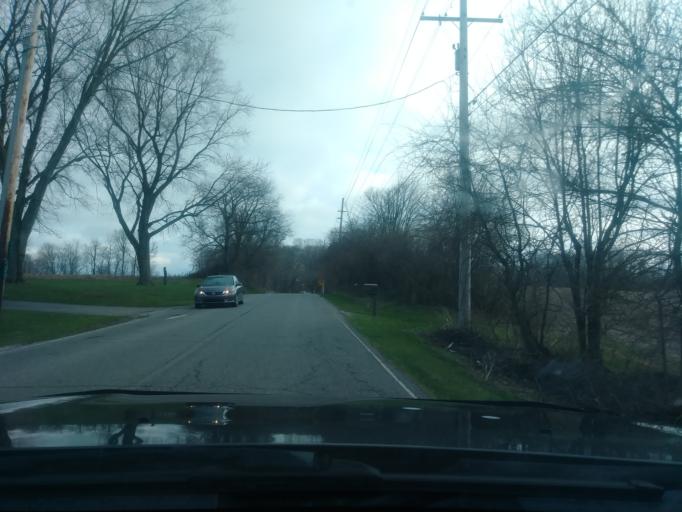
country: US
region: Indiana
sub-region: LaPorte County
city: LaPorte
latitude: 41.6173
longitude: -86.7964
